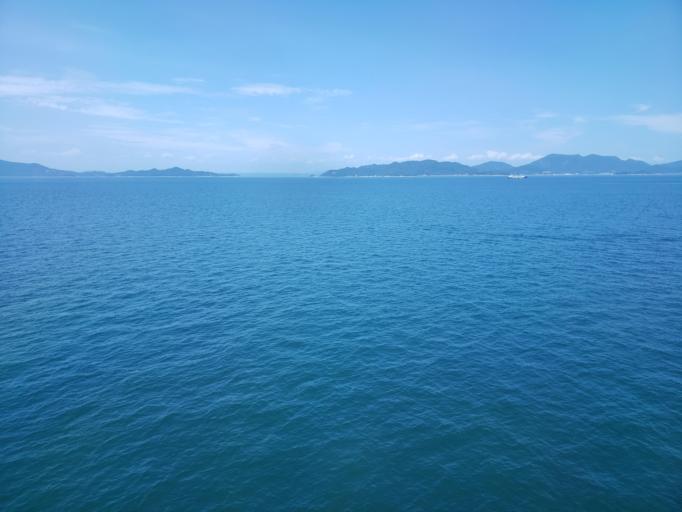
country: JP
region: Kagawa
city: Tonosho
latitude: 34.4056
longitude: 134.1490
